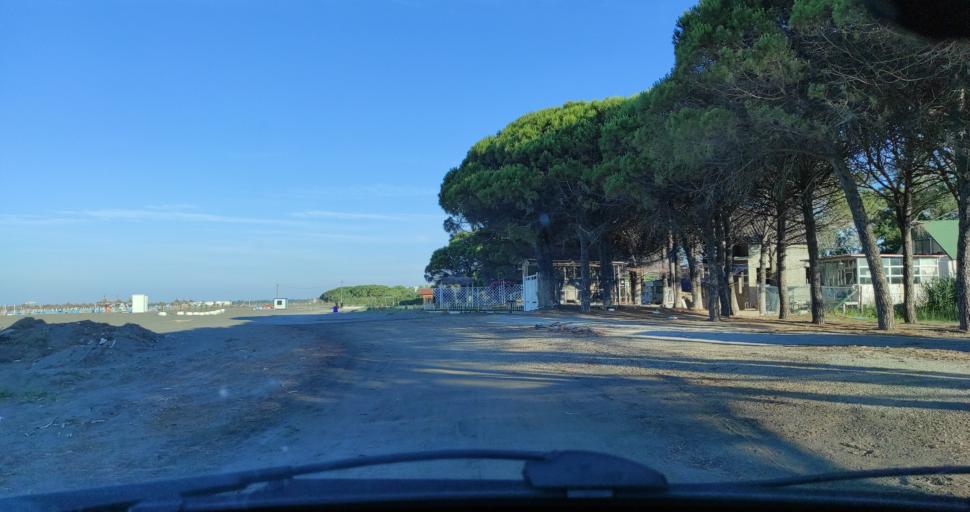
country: AL
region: Shkoder
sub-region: Rrethi i Shkodres
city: Velipoje
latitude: 41.8600
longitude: 19.4393
